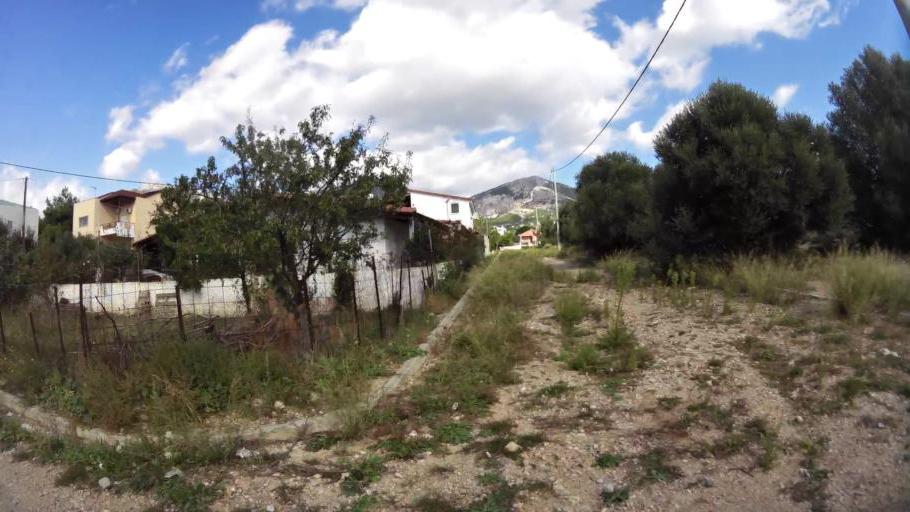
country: GR
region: Attica
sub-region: Nomarchia Anatolikis Attikis
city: Thrakomakedones
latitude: 38.1244
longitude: 23.7485
